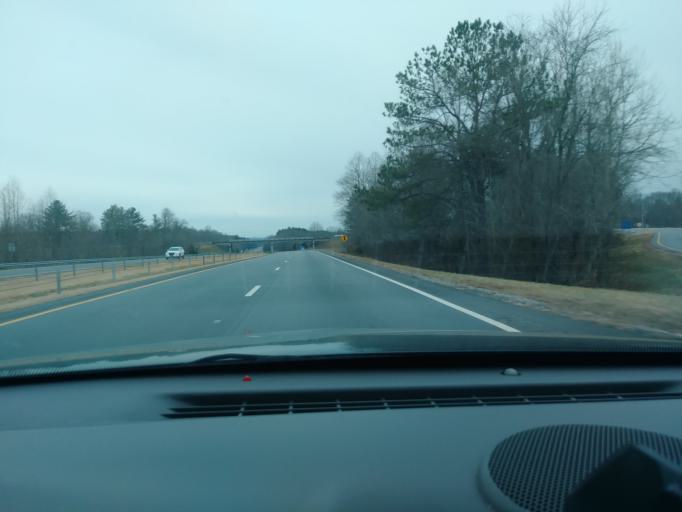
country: US
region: North Carolina
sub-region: Wilkes County
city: North Wilkesboro
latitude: 36.1372
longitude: -81.1003
